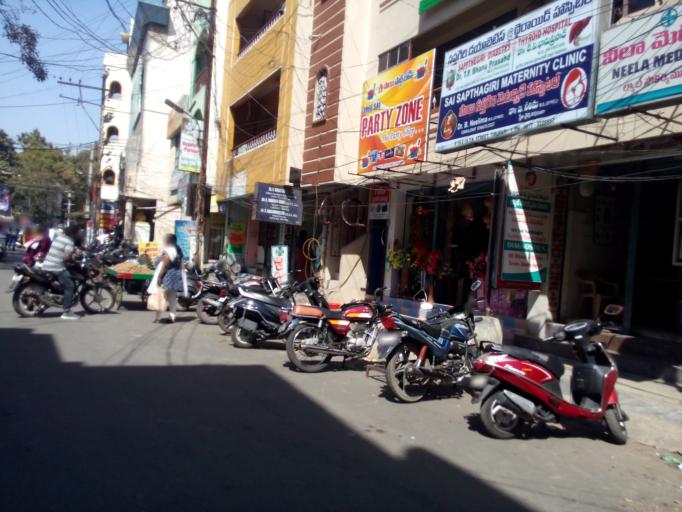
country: IN
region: Andhra Pradesh
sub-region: Chittoor
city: Tirupati
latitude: 13.6359
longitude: 79.4181
